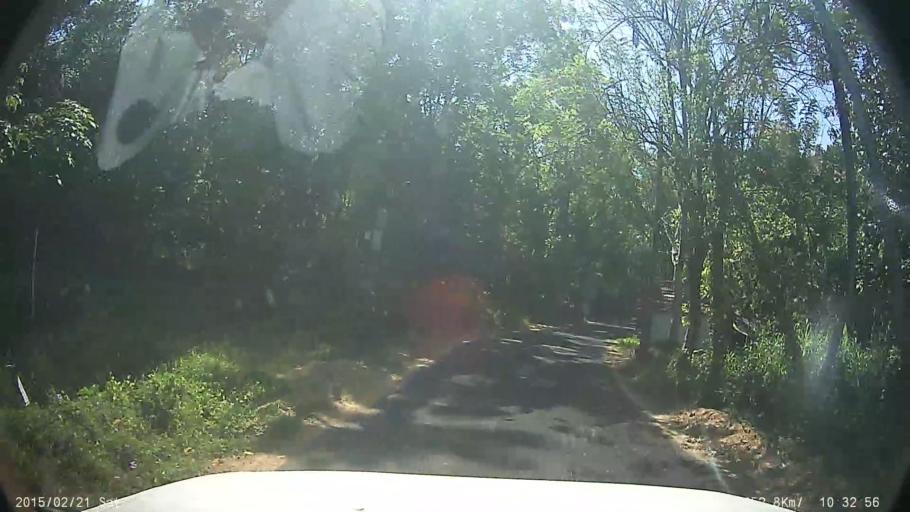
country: IN
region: Kerala
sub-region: Kottayam
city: Lalam
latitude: 9.8380
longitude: 76.7123
